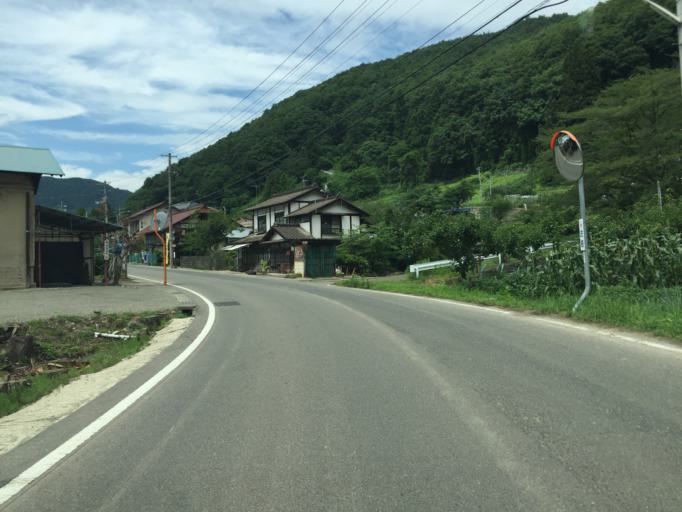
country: JP
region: Fukushima
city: Fukushima-shi
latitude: 37.8293
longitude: 140.4042
